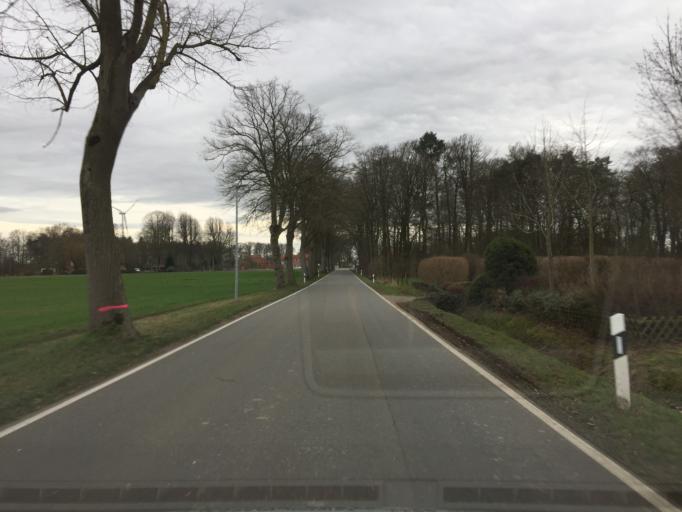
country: DE
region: Lower Saxony
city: Schwaforden
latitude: 52.7525
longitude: 8.8323
